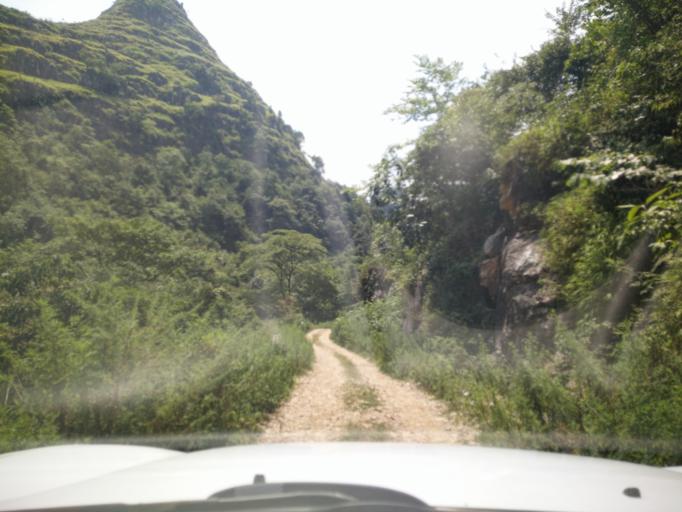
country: CN
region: Guangxi Zhuangzu Zizhiqu
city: Xinzhou
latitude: 25.0135
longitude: 105.7048
